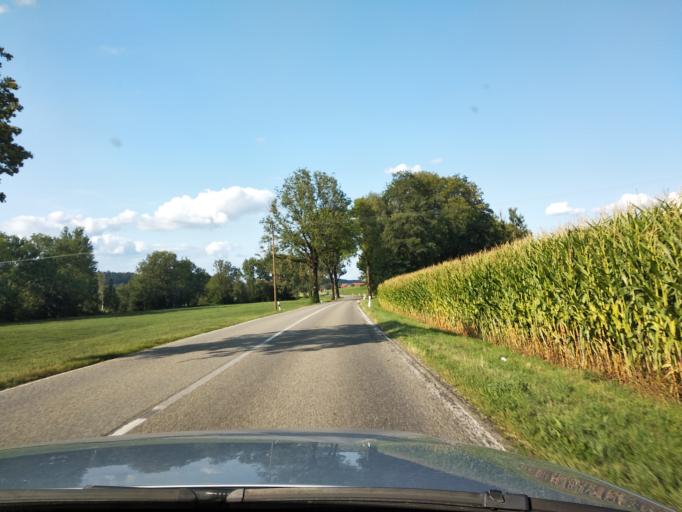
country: DE
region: Baden-Wuerttemberg
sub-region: Tuebingen Region
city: Leutkirch im Allgau
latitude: 47.8615
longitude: 10.0310
